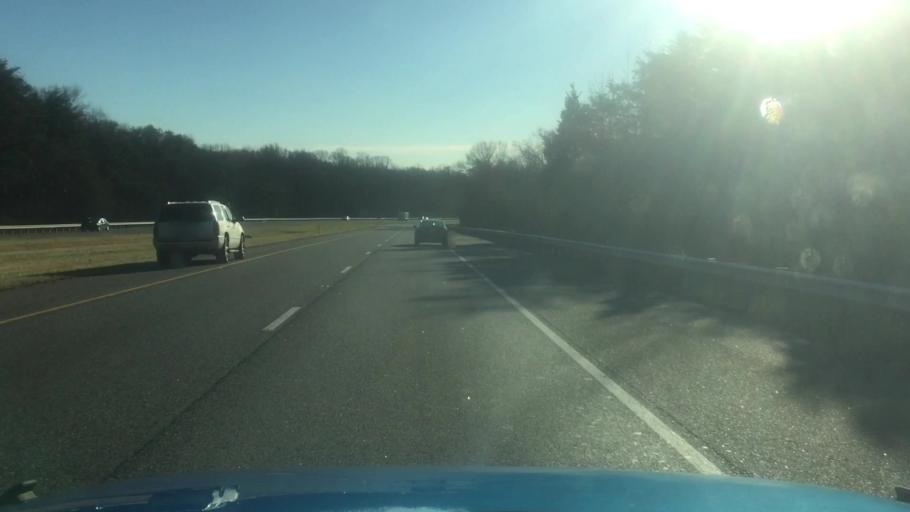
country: US
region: Maryland
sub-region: Prince George's County
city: Berwyn Heights
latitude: 38.9855
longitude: -76.9089
